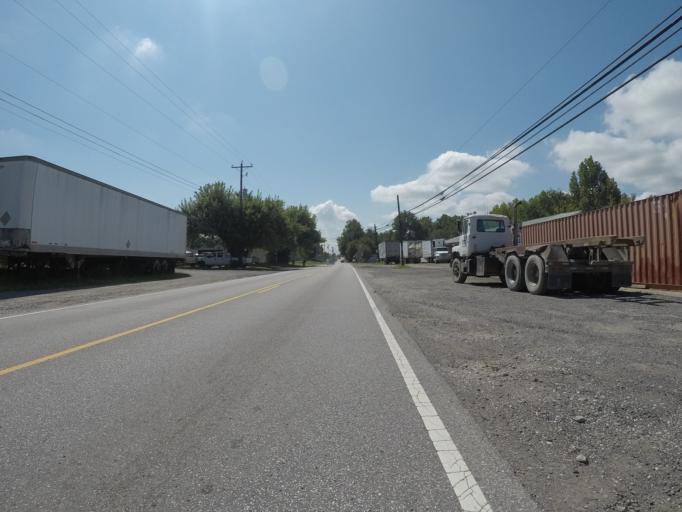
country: US
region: Ohio
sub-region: Lawrence County
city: South Point
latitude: 38.4482
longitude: -82.5940
